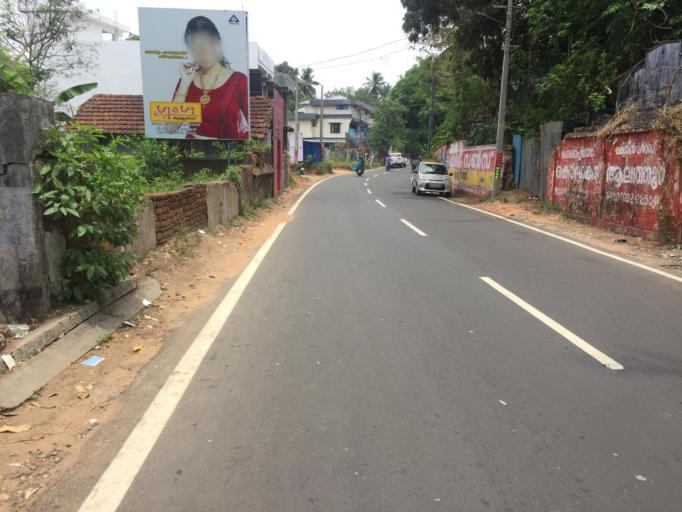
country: IN
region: Kerala
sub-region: Palakkad district
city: Chittur
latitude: 10.7021
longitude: 76.7394
